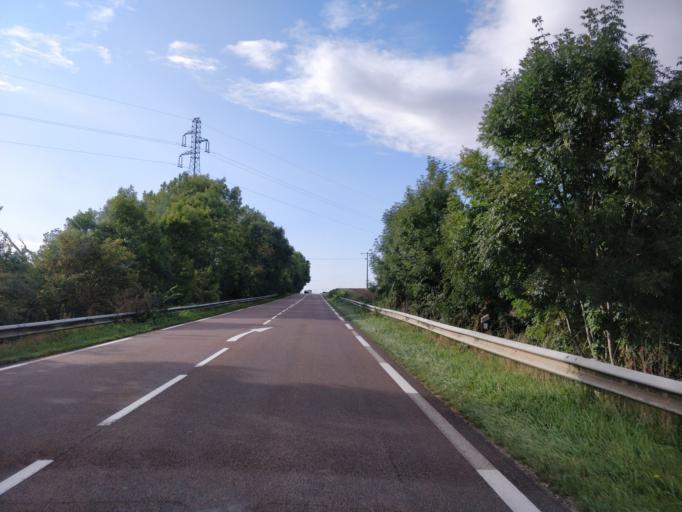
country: FR
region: Champagne-Ardenne
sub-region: Departement de l'Aube
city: Lusigny-sur-Barse
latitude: 48.2703
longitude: 4.2096
